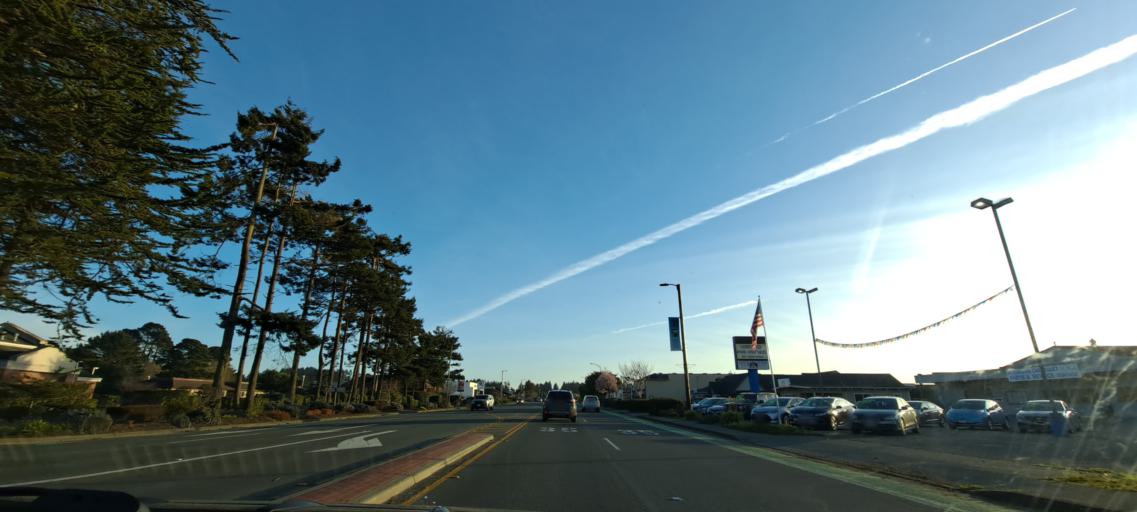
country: US
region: California
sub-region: Humboldt County
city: McKinleyville
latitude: 40.9393
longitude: -124.1011
